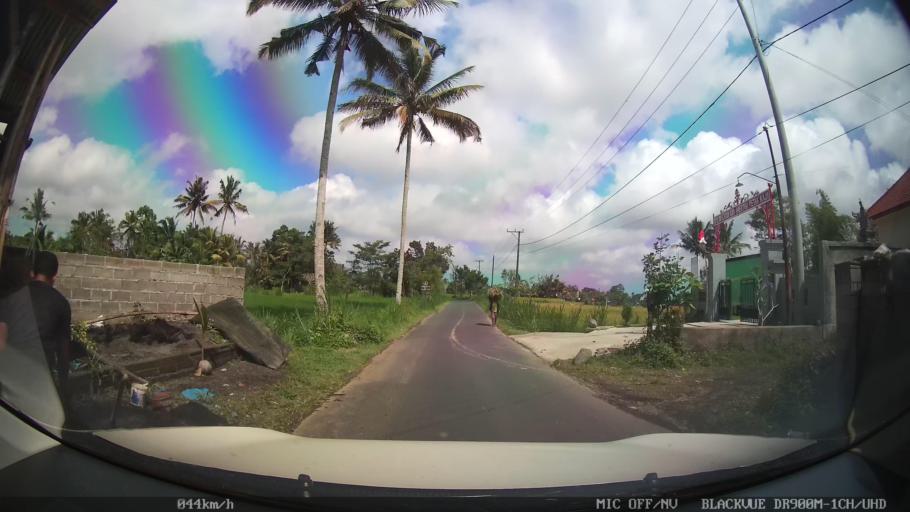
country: ID
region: Bali
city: Banjar Abuan
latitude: -8.4616
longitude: 115.3237
